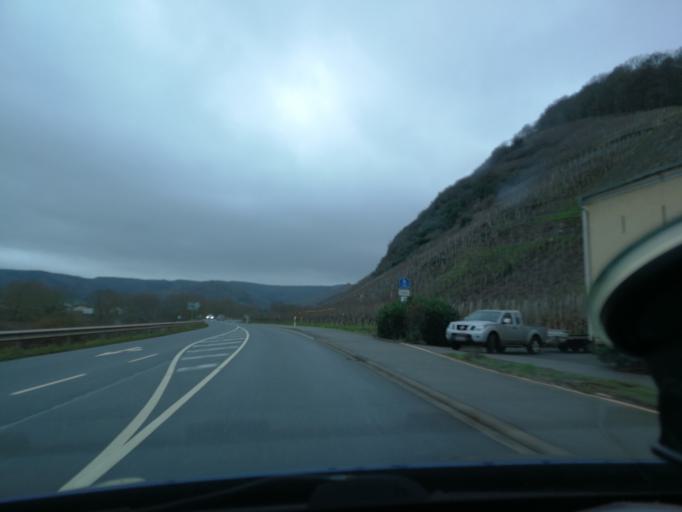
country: DE
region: Rheinland-Pfalz
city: Klusserath
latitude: 49.8411
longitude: 6.8450
